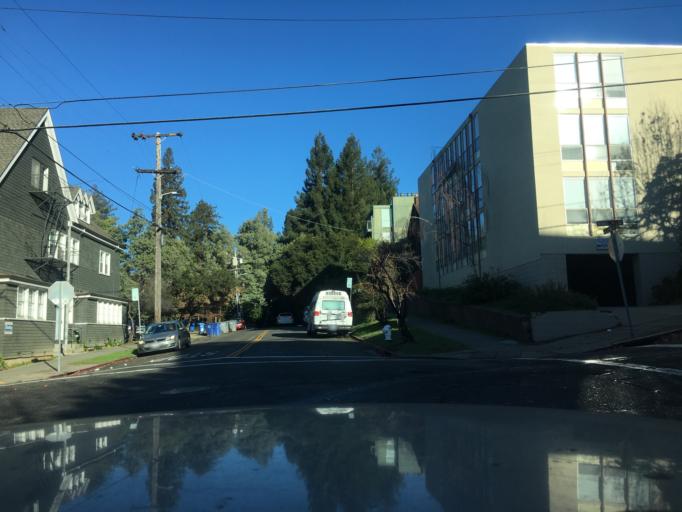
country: US
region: California
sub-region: Alameda County
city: Berkeley
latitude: 37.8764
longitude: -122.2570
